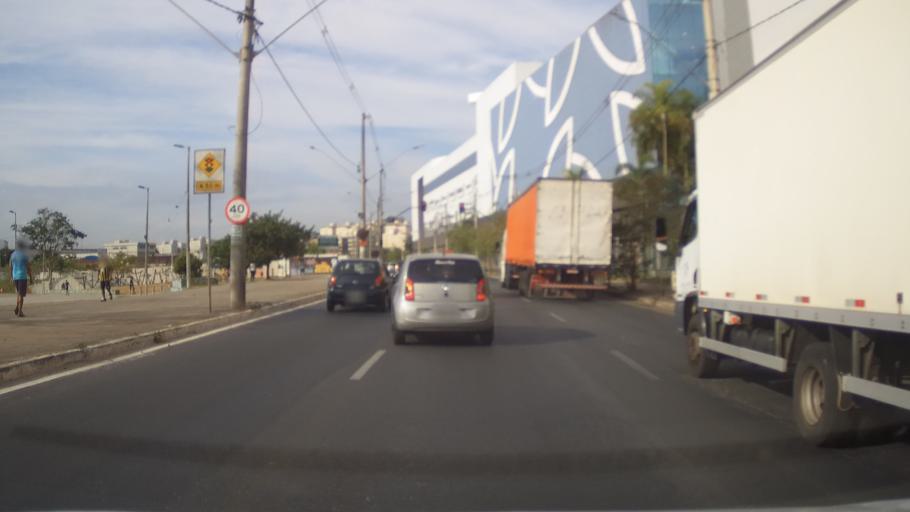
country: BR
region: Minas Gerais
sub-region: Contagem
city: Contagem
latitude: -19.8801
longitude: -44.0372
